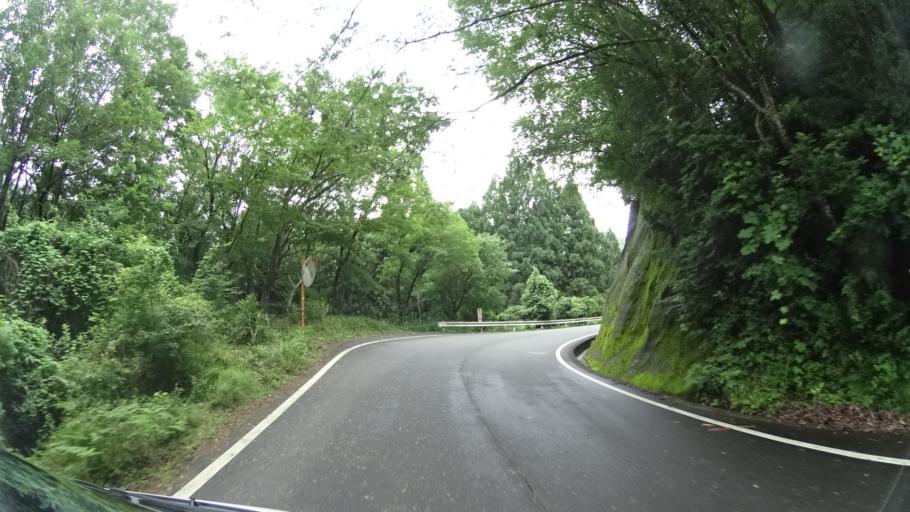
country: JP
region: Kyoto
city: Kameoka
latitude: 35.0511
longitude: 135.4257
